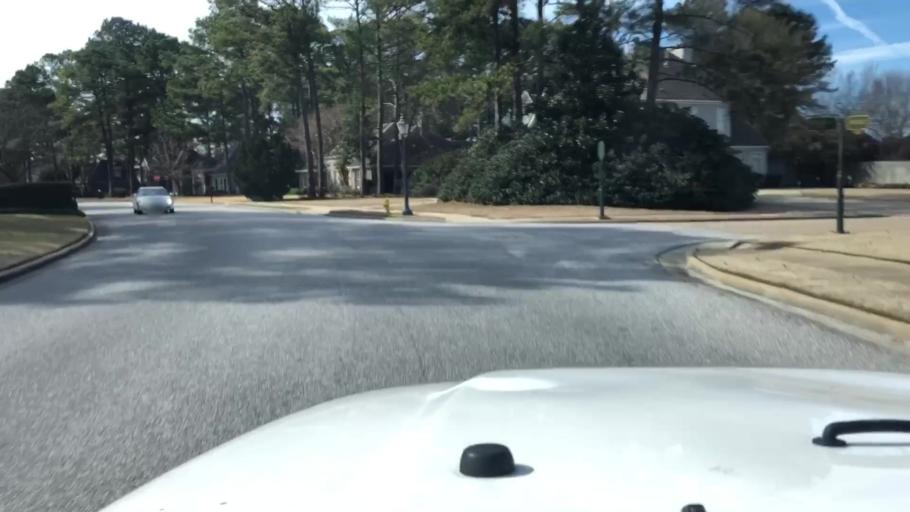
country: US
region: Alabama
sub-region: Montgomery County
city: Pike Road
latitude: 32.3590
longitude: -86.1464
